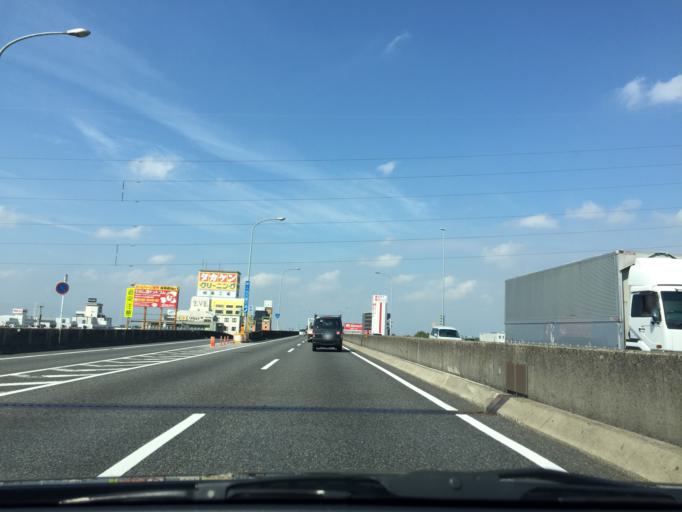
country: JP
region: Gifu
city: Kasamatsucho
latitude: 35.3882
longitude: 136.7893
